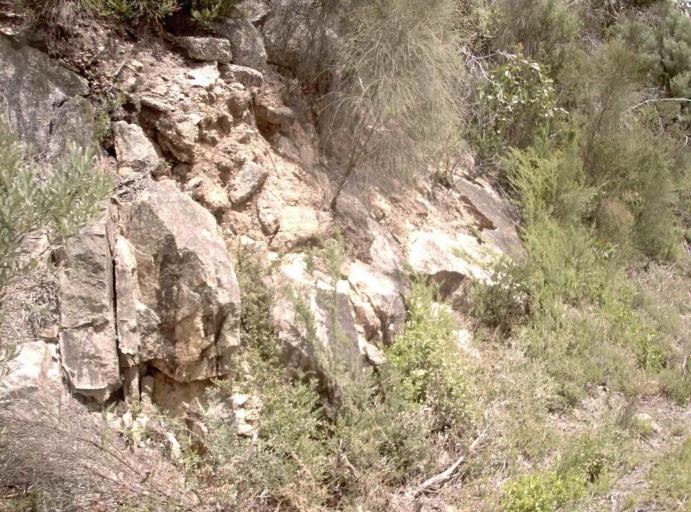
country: AU
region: Victoria
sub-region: Latrobe
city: Morwell
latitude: -39.0136
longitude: 146.2987
